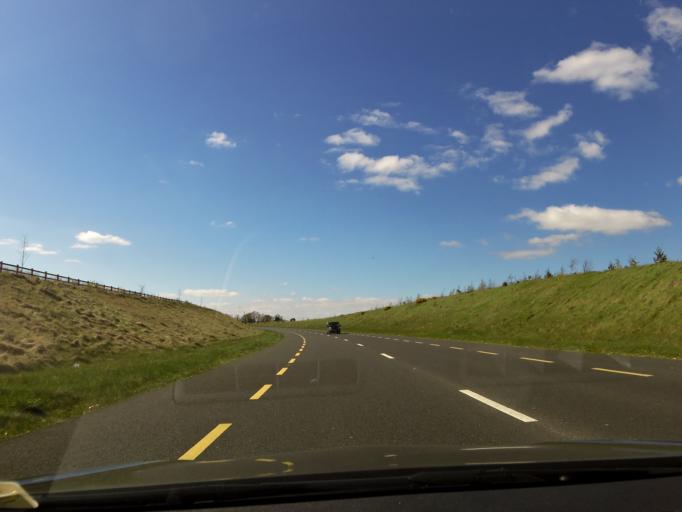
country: IE
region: Leinster
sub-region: Kildare
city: Athy
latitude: 52.9941
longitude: -6.9522
